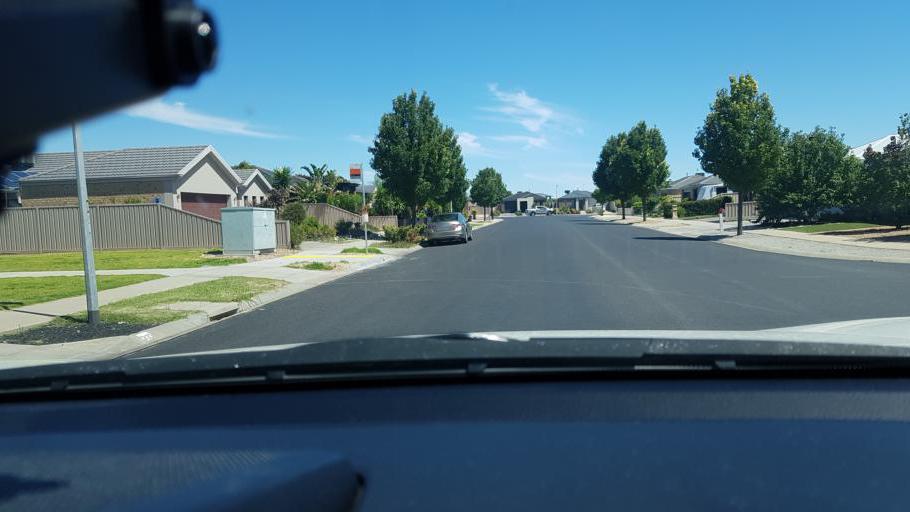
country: AU
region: Victoria
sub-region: Horsham
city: Horsham
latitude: -36.7122
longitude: 142.1805
